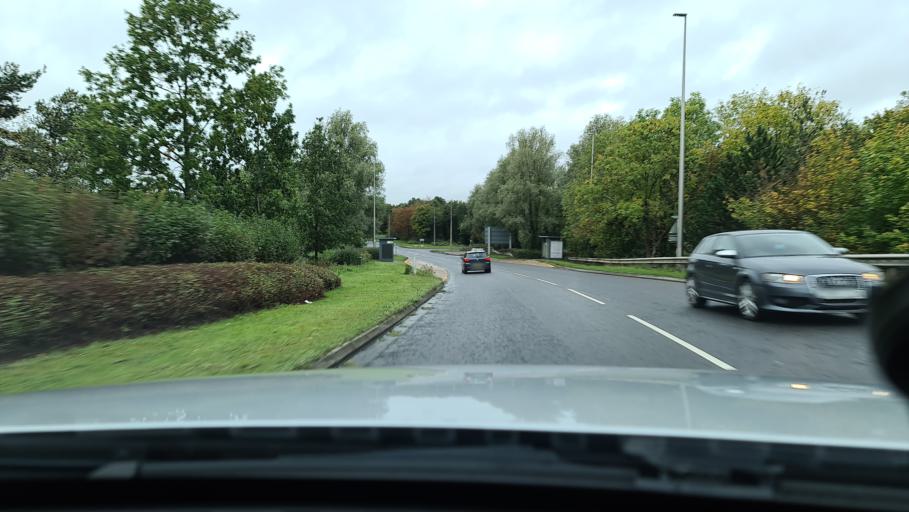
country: GB
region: England
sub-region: Milton Keynes
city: Bradwell
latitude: 52.0489
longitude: -0.8046
